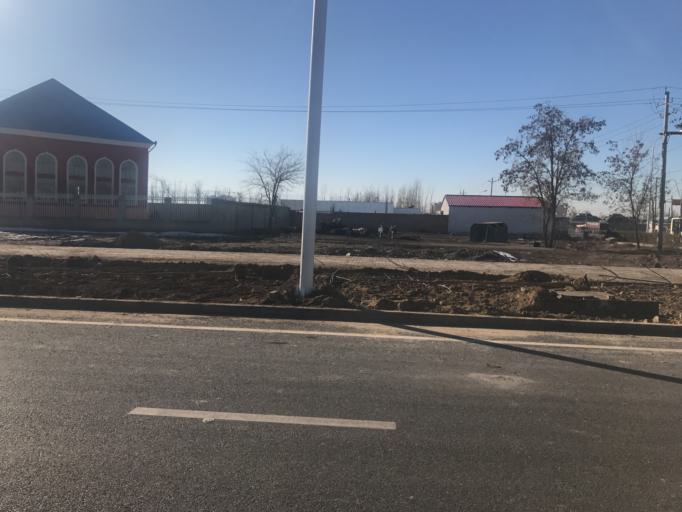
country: CN
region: Xinjiang Uygur Zizhiqu
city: Ailan Mubage
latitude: 43.9509
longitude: 81.3544
